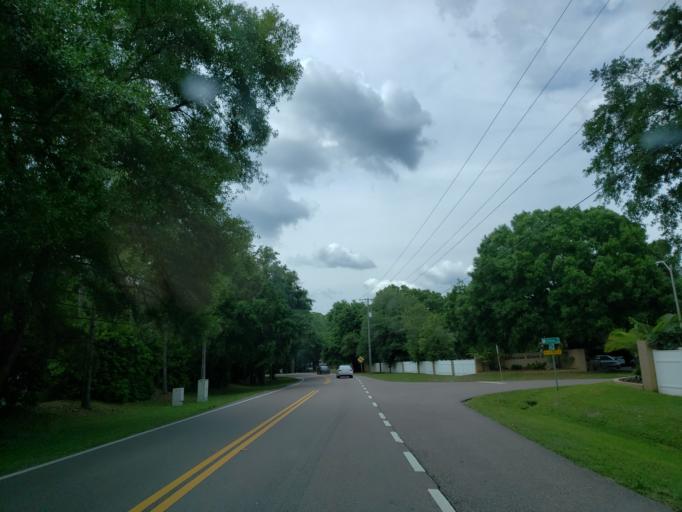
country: US
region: Florida
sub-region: Hillsborough County
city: Citrus Park
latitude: 28.1117
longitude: -82.6037
